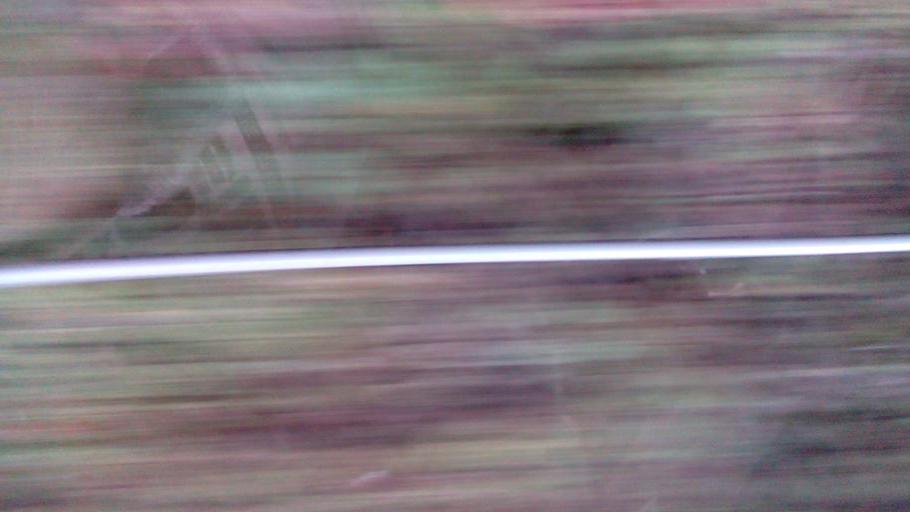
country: TW
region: Taiwan
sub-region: Hualien
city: Hualian
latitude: 24.3499
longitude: 121.3245
